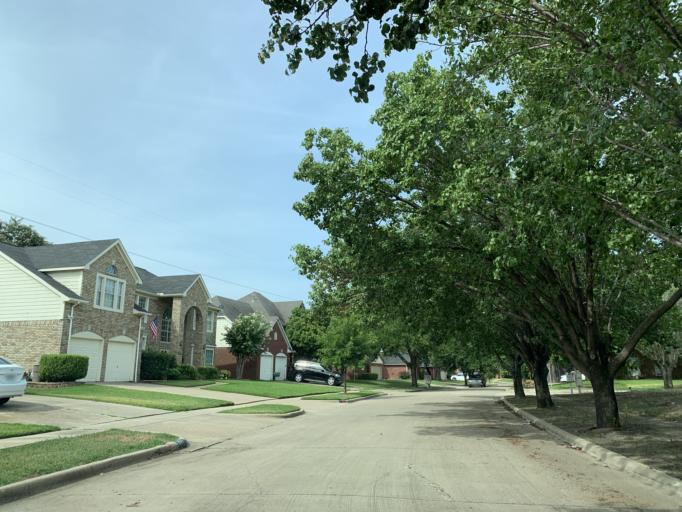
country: US
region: Texas
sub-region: Dallas County
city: Grand Prairie
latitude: 32.6615
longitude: -97.0107
